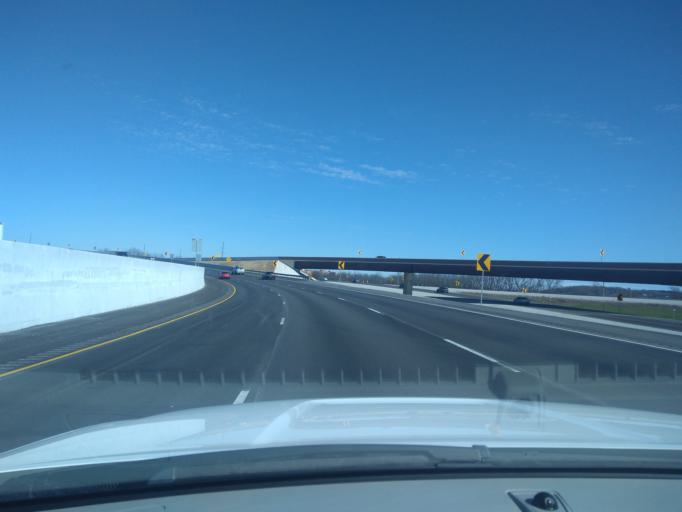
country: US
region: Arkansas
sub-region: Washington County
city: Johnson
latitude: 36.1073
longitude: -94.1730
